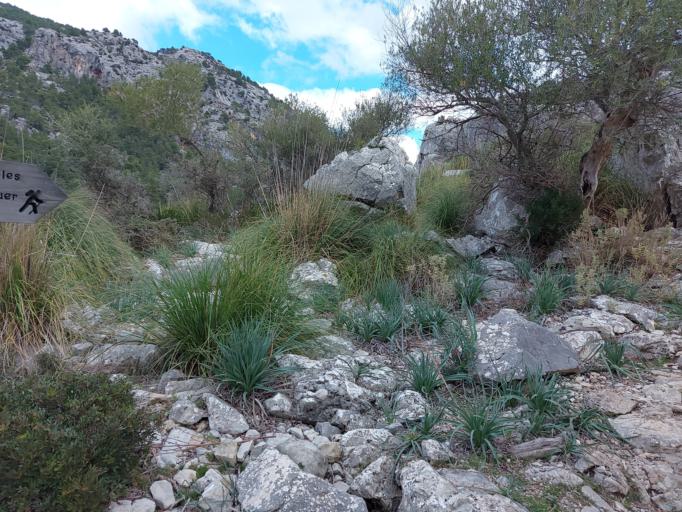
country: ES
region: Balearic Islands
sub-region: Illes Balears
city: Mancor de la Vall
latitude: 39.7699
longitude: 2.8195
